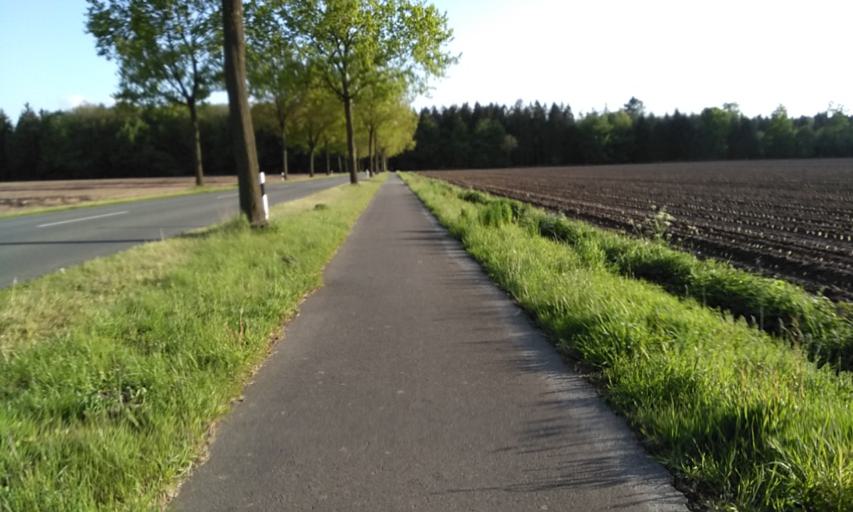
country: DE
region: Lower Saxony
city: Wohnste
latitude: 53.4028
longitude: 9.5421
